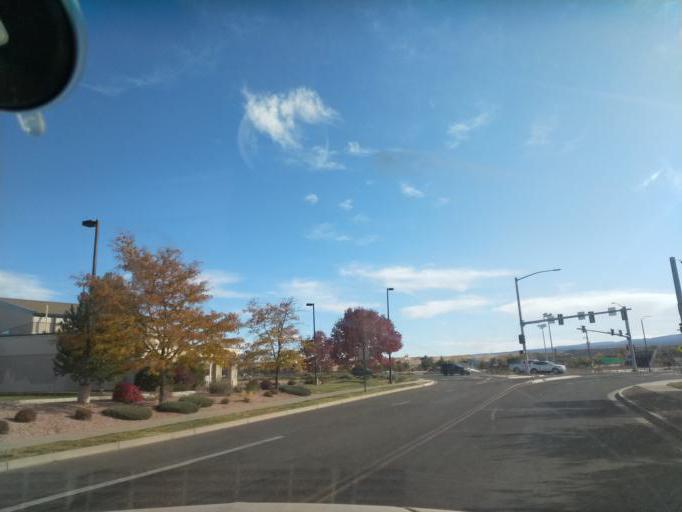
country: US
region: Colorado
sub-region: Mesa County
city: Orchard Mesa
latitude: 39.0395
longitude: -108.5390
